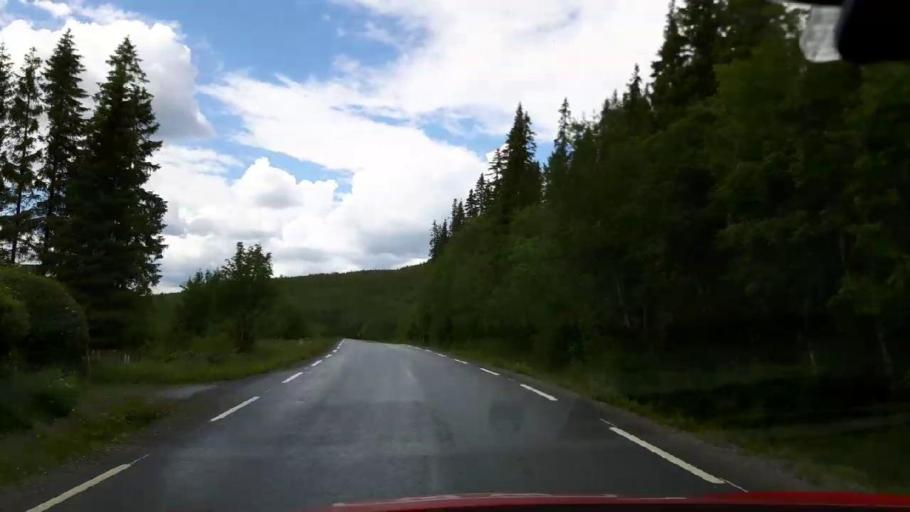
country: NO
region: Nord-Trondelag
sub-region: Lierne
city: Sandvika
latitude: 64.1148
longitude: 13.9691
